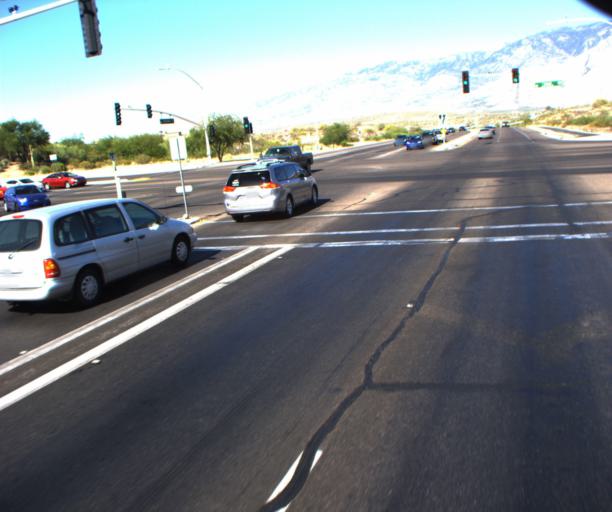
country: US
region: Arizona
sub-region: Pima County
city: Oro Valley
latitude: 32.4243
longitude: -110.9614
